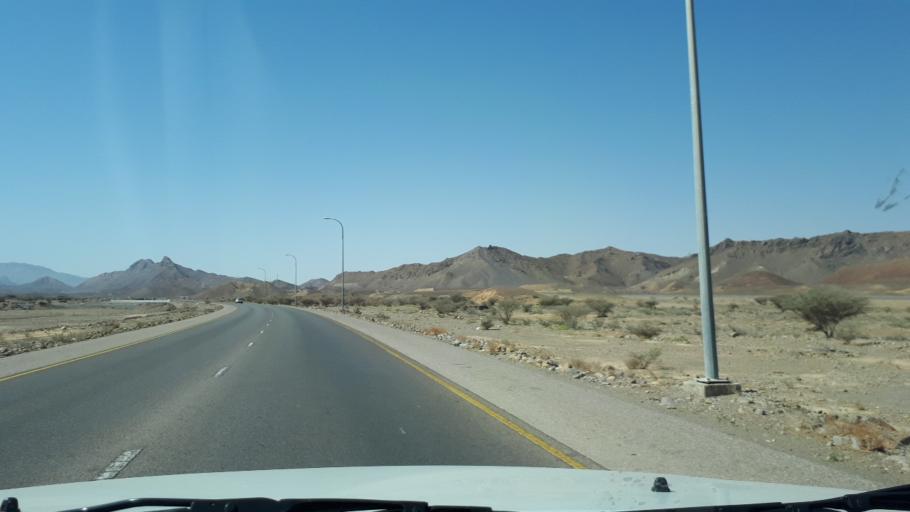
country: OM
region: Ash Sharqiyah
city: Sur
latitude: 22.3625
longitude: 59.3125
